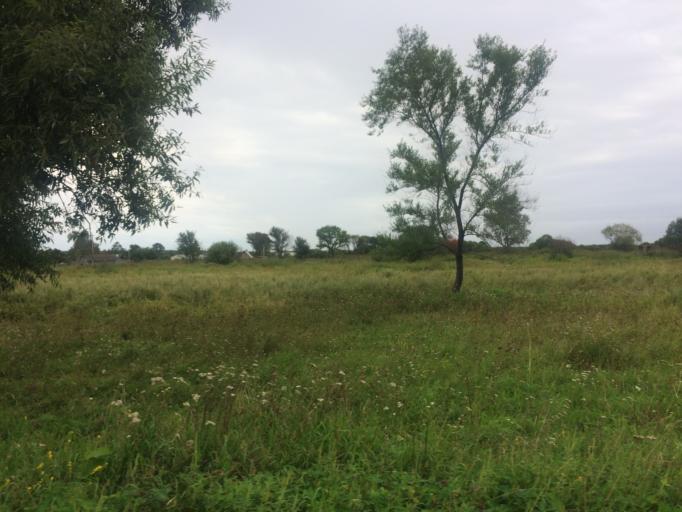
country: RU
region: Primorskiy
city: Lazo
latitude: 45.8306
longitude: 133.6127
